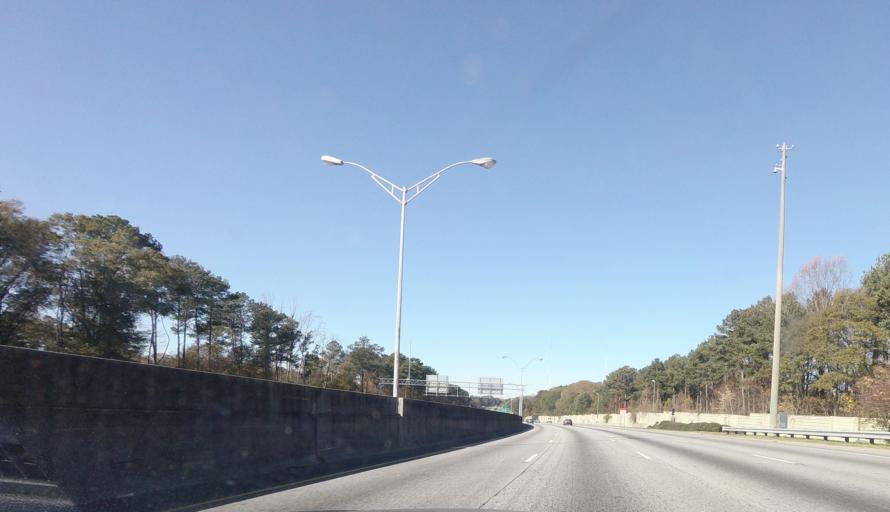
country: US
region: Georgia
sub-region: Fulton County
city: Atlanta
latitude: 33.7581
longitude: -84.4712
